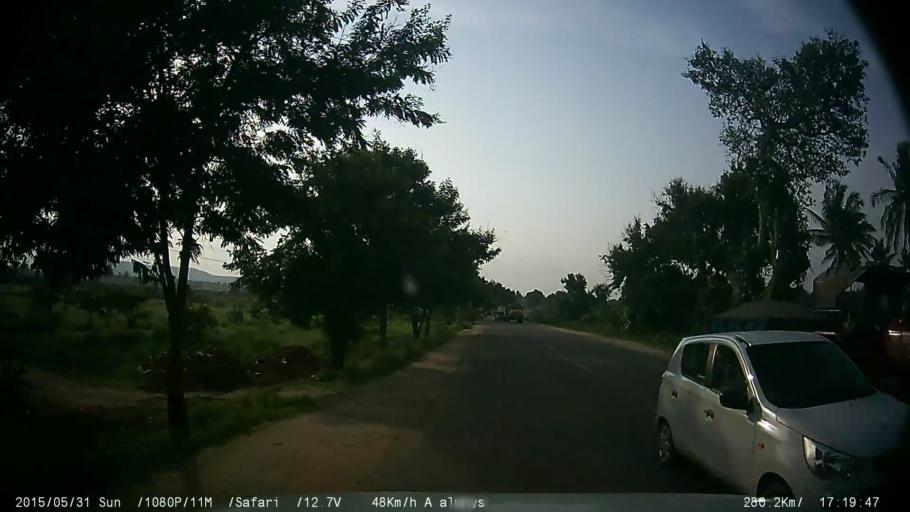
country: IN
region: Karnataka
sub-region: Chamrajnagar
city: Gundlupet
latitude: 11.8180
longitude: 76.6839
